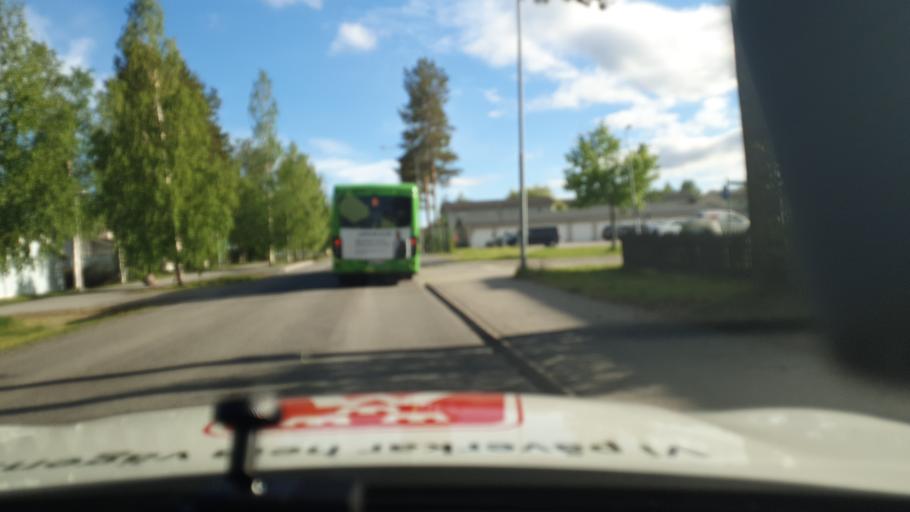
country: SE
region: Vaesterbotten
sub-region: Umea Kommun
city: Ersmark
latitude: 63.8624
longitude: 20.3378
